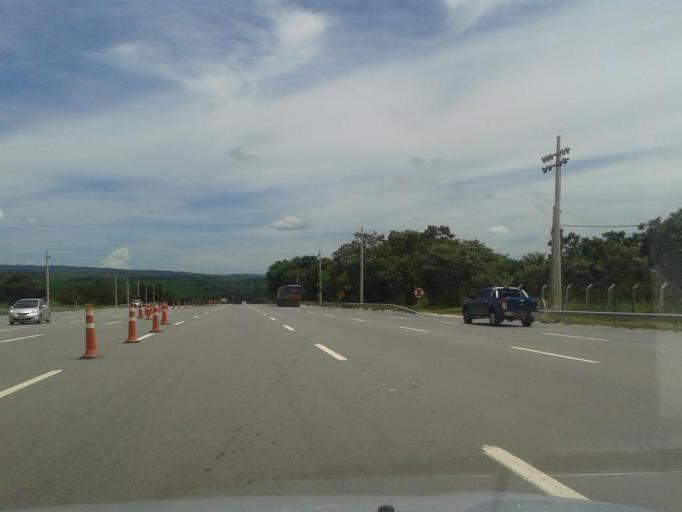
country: BR
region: Goias
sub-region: Hidrolandia
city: Hidrolandia
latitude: -17.1625
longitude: -49.2129
